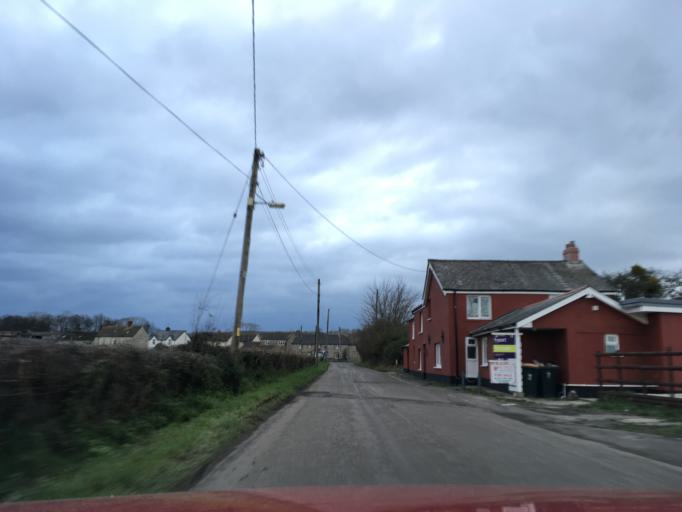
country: GB
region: Wales
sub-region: Newport
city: Bishton
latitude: 51.5818
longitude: -2.8783
